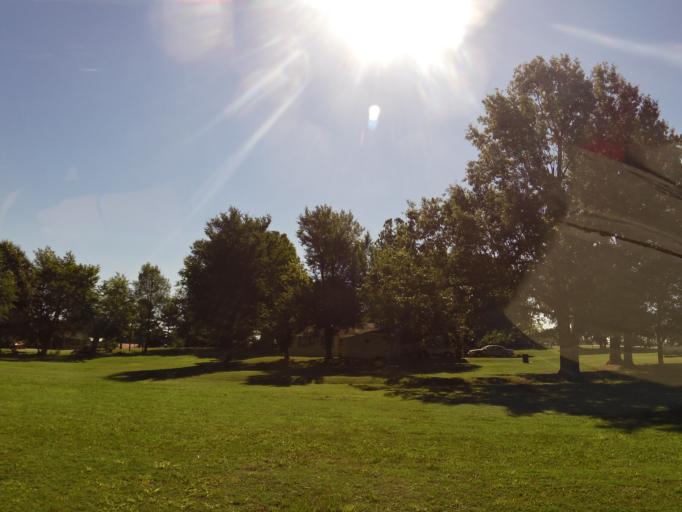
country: US
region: Arkansas
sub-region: Clay County
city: Piggott
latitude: 36.4277
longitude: -90.2714
